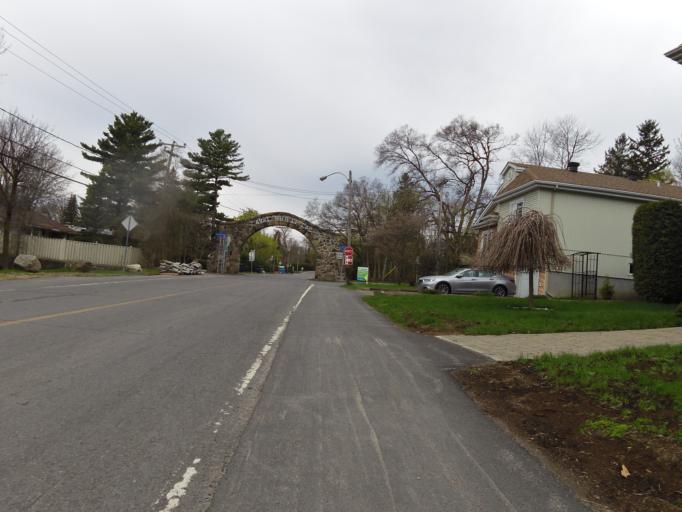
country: CA
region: Quebec
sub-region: Laurentides
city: Deux-Montagnes
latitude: 45.5226
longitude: -73.8638
